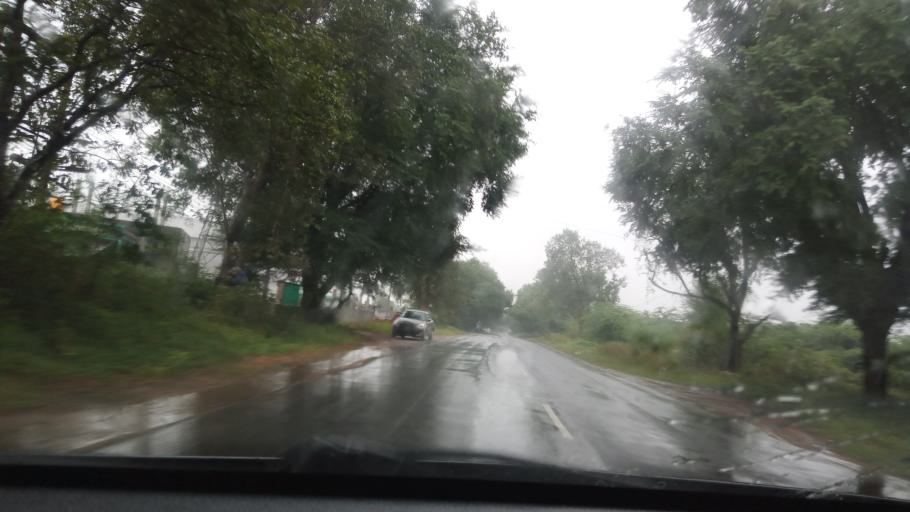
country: IN
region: Tamil Nadu
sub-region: Vellore
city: Walajapet
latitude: 12.8509
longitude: 79.3884
